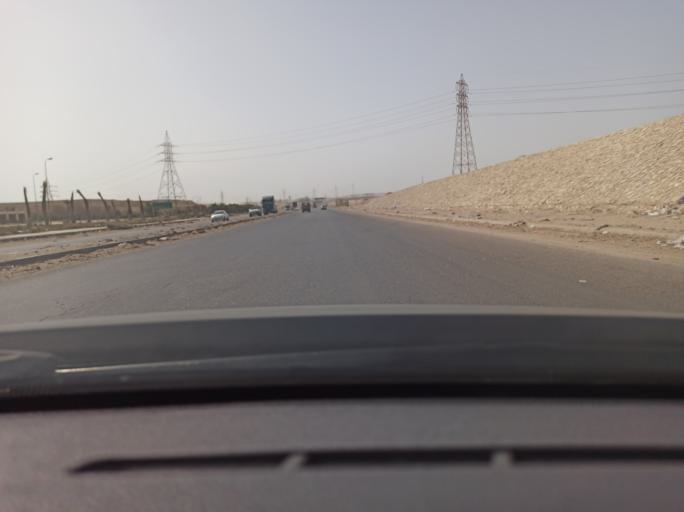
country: EG
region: Muhafazat al Qahirah
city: Halwan
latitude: 29.8011
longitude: 31.3504
